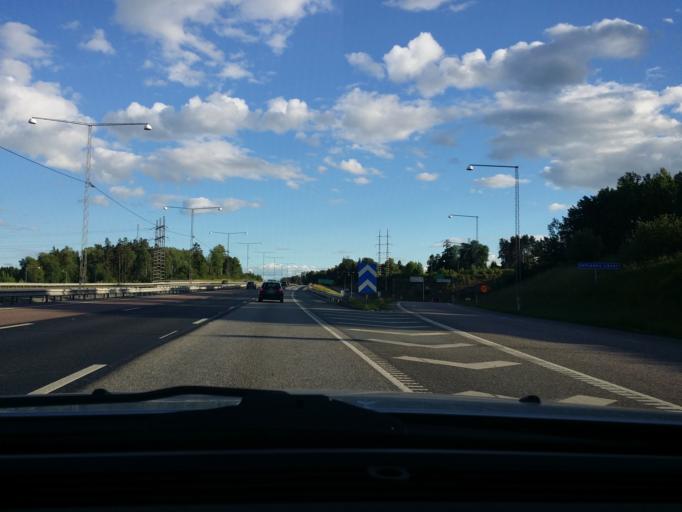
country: SE
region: Stockholm
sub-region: Upplands Vasby Kommun
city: Upplands Vaesby
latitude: 59.4973
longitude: 17.9235
